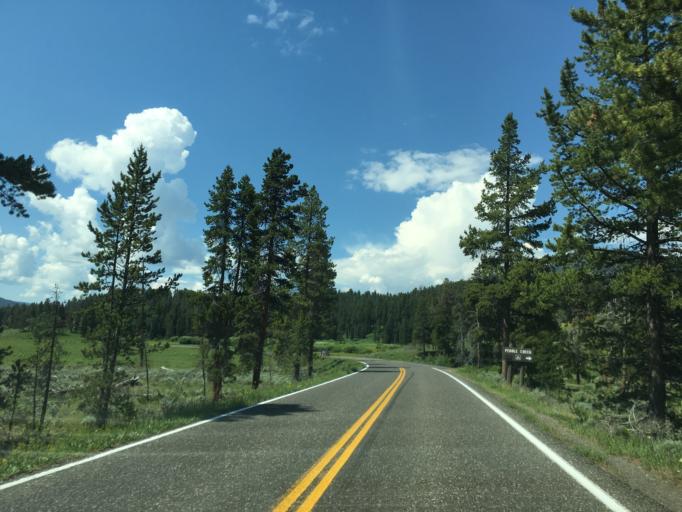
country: US
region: Montana
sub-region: Park County
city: Livingston
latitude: 44.9148
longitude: -110.1123
